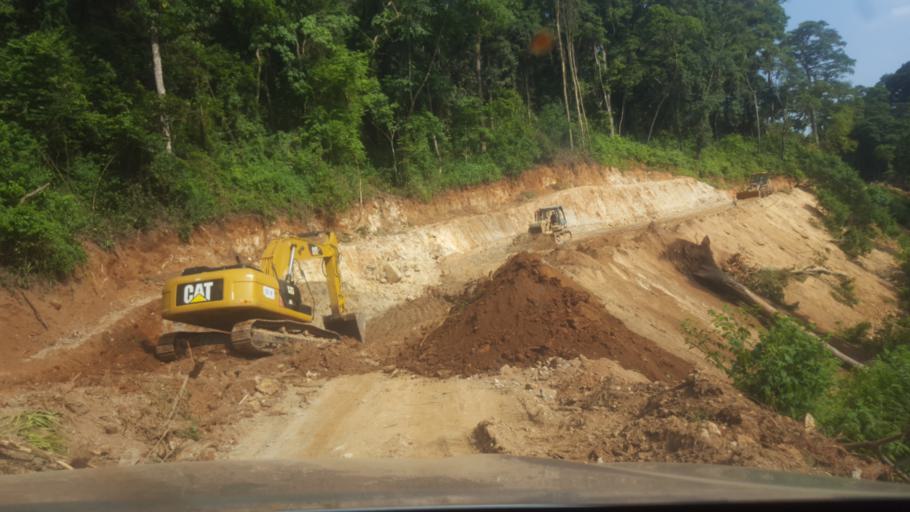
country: ET
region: Southern Nations, Nationalities, and People's Region
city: Tippi
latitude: 7.5373
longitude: 34.9813
